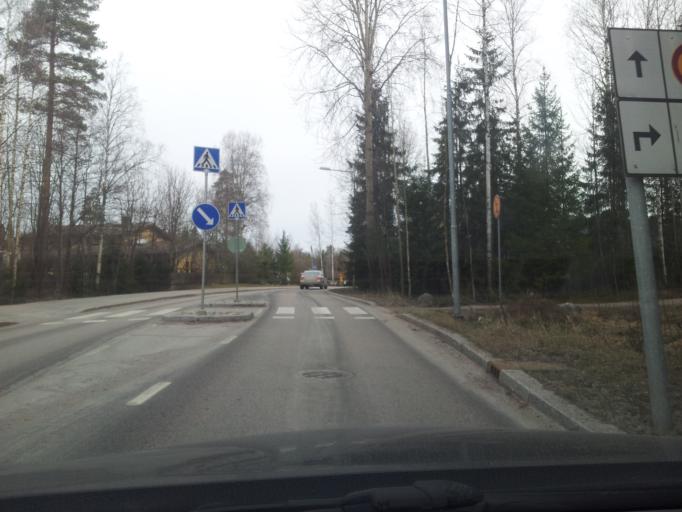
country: FI
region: Uusimaa
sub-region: Helsinki
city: Otaniemi
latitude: 60.1893
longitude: 24.7970
